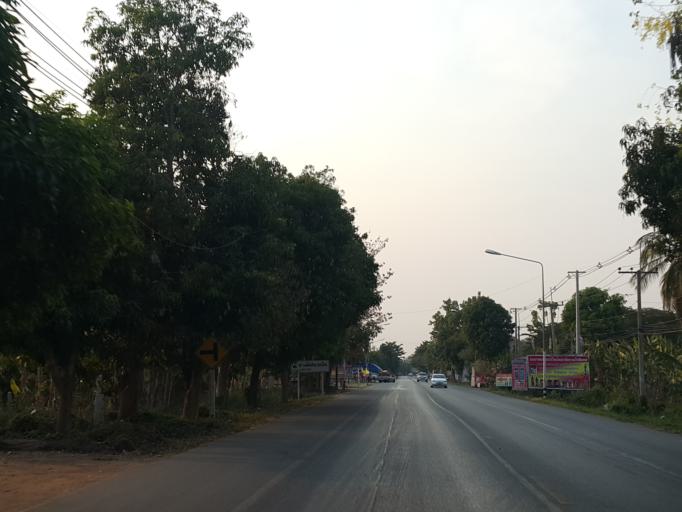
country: TH
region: Sukhothai
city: Si Samrong
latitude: 17.2231
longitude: 99.8610
